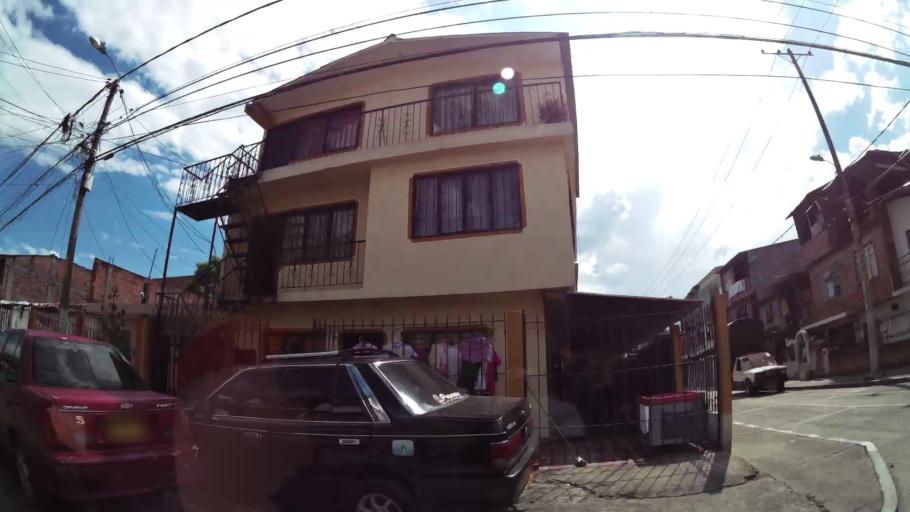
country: CO
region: Valle del Cauca
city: Cali
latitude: 3.4006
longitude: -76.5160
